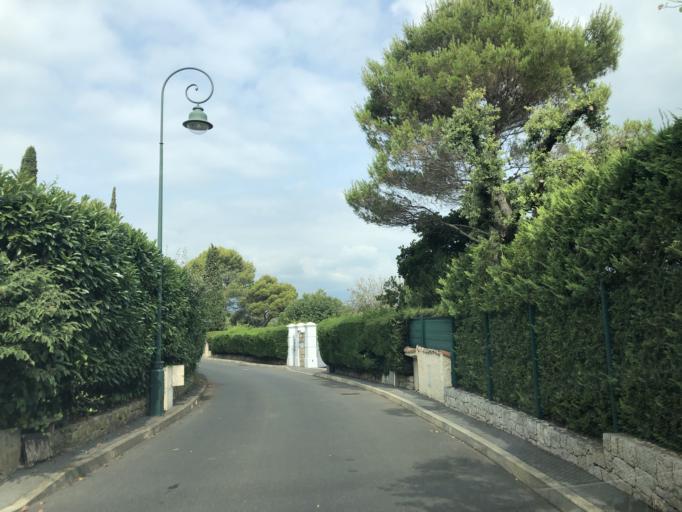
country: FR
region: Provence-Alpes-Cote d'Azur
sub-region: Departement des Alpes-Maritimes
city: Biot
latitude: 43.6270
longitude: 7.0839
